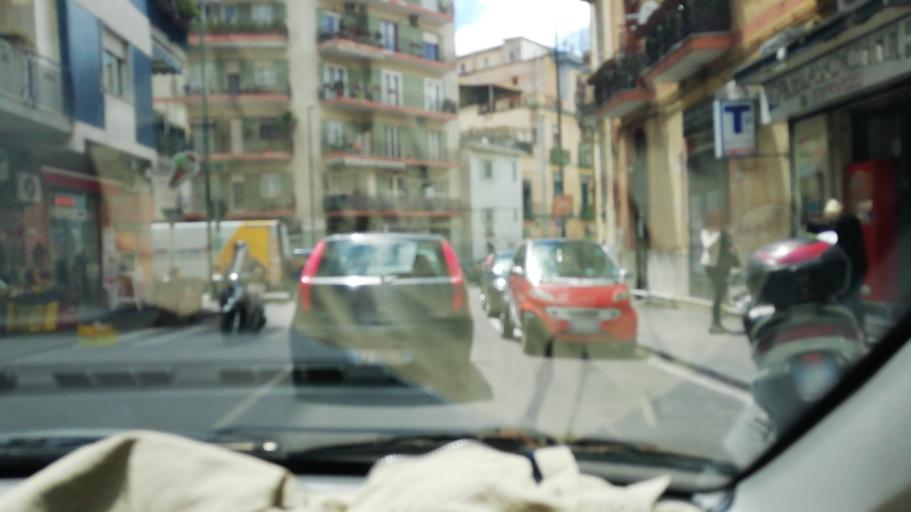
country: IT
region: Campania
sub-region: Provincia di Napoli
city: Napoli
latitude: 40.8497
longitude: 14.2201
